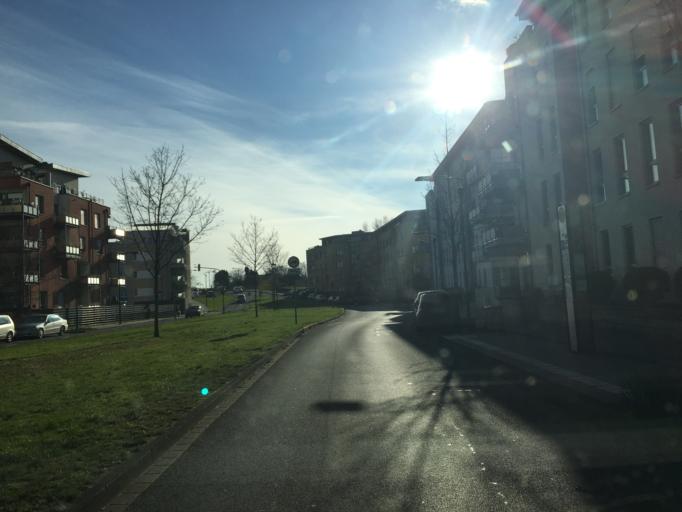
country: DE
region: North Rhine-Westphalia
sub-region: Regierungsbezirk Koln
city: Hurth
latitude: 50.8770
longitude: 6.8828
